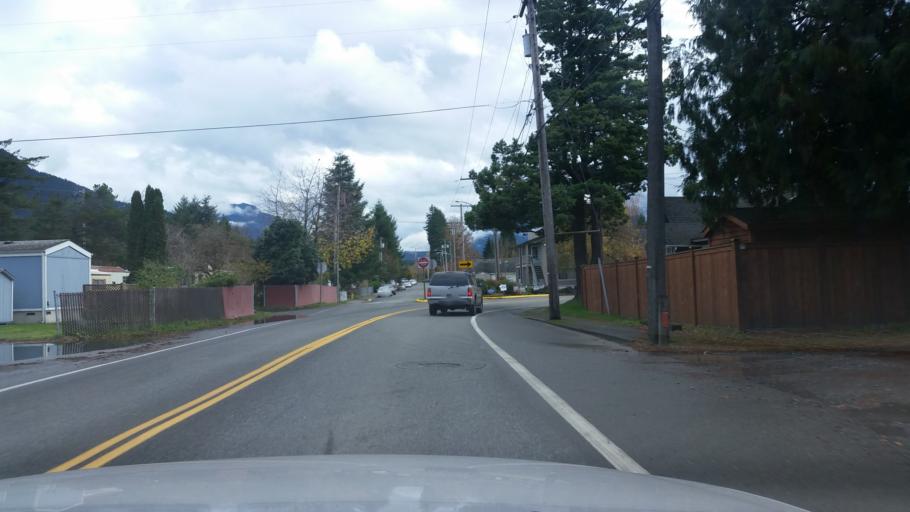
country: US
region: Washington
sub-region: King County
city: North Bend
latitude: 47.4982
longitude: -121.7853
